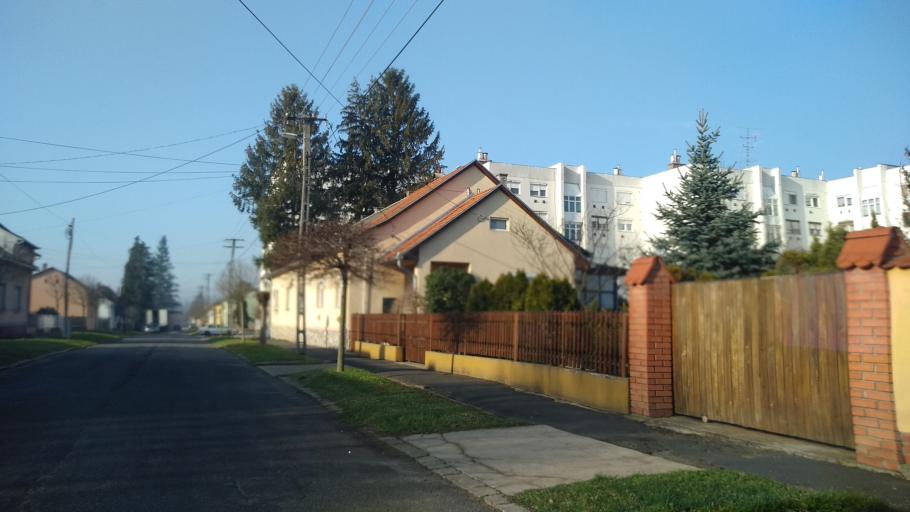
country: HU
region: Somogy
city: Barcs
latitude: 45.9581
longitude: 17.4610
